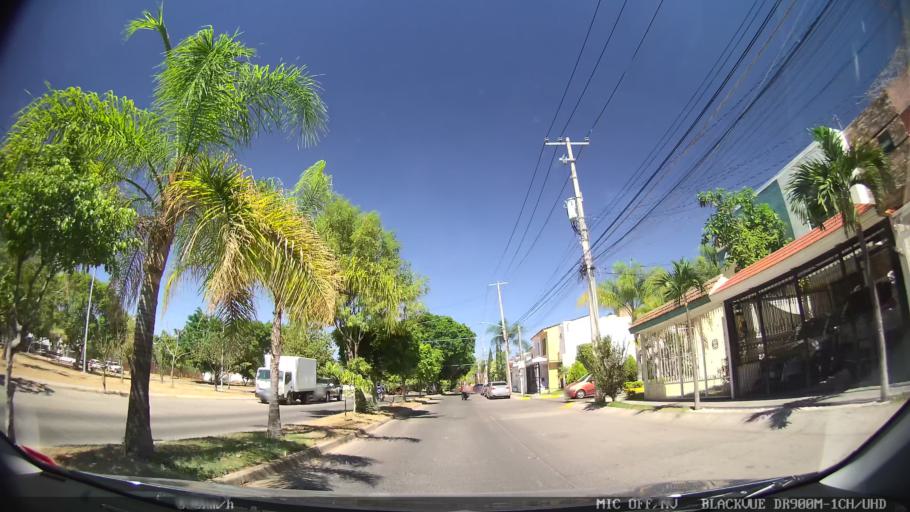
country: MX
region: Jalisco
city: Tlaquepaque
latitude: 20.6470
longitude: -103.2858
